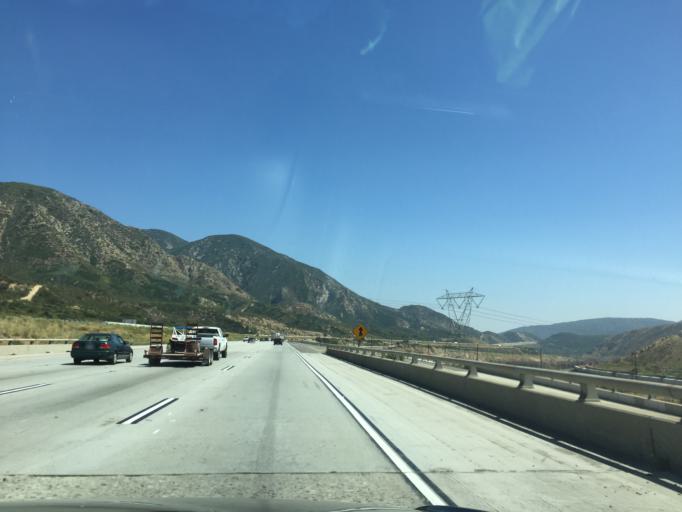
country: US
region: California
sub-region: San Bernardino County
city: Oak Hills
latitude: 34.2973
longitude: -117.4568
